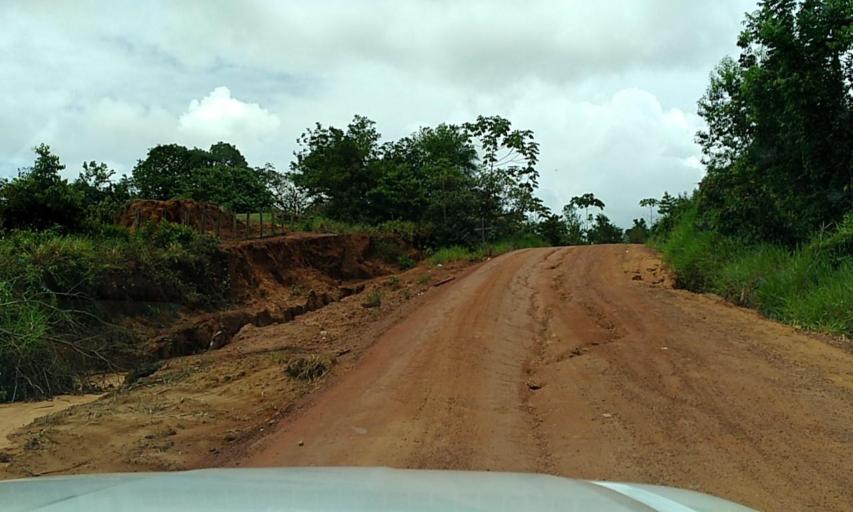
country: BR
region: Para
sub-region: Senador Jose Porfirio
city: Senador Jose Porfirio
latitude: -2.6154
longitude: -51.8716
